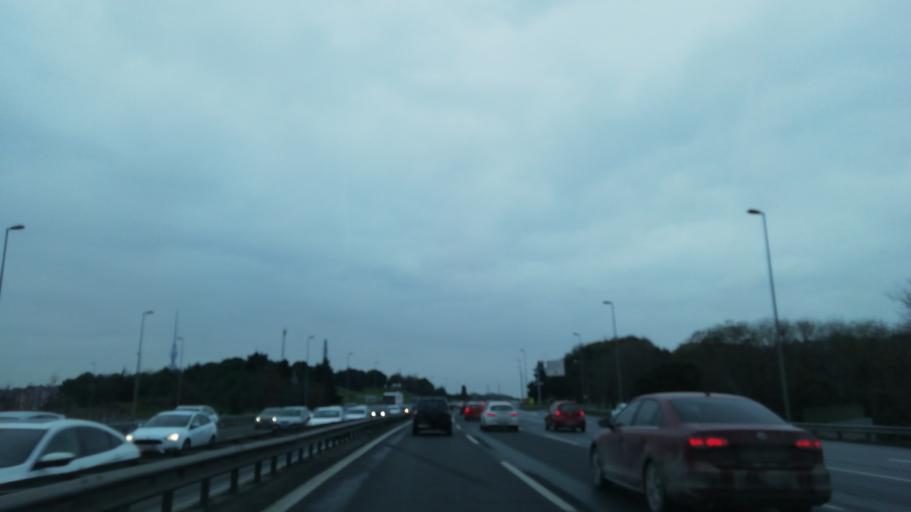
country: TR
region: Istanbul
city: UEskuedar
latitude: 41.0349
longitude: 29.0444
